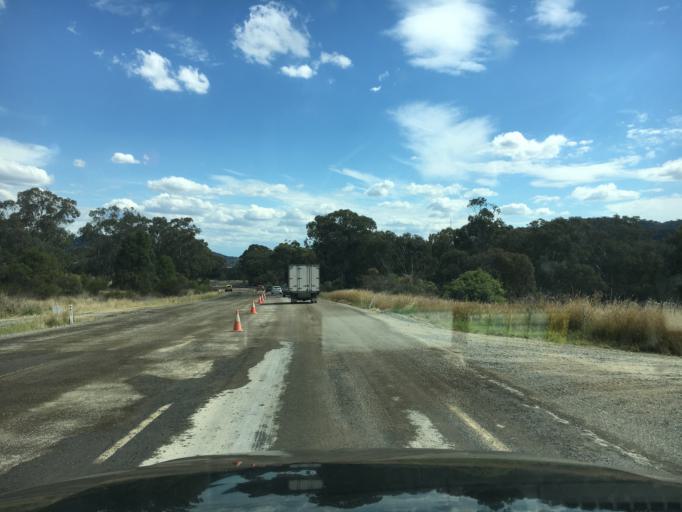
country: AU
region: New South Wales
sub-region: Liverpool Plains
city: Quirindi
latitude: -31.4513
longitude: 150.8633
